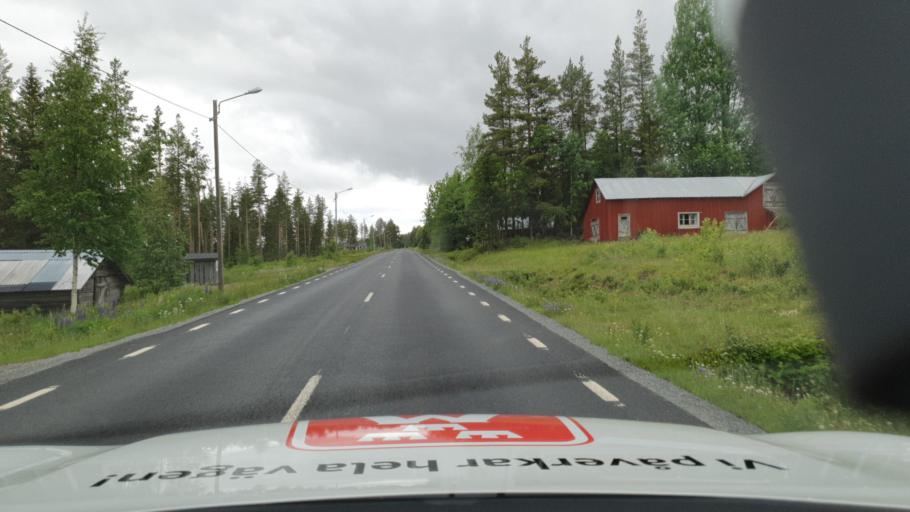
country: SE
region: Vaesterbotten
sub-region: Dorotea Kommun
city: Dorotea
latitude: 64.2302
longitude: 16.5430
